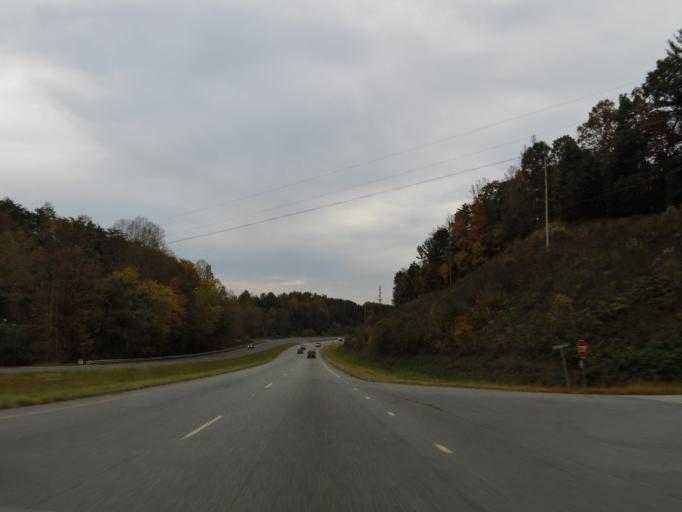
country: US
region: North Carolina
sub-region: Caldwell County
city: Lenoir
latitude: 35.9509
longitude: -81.5511
